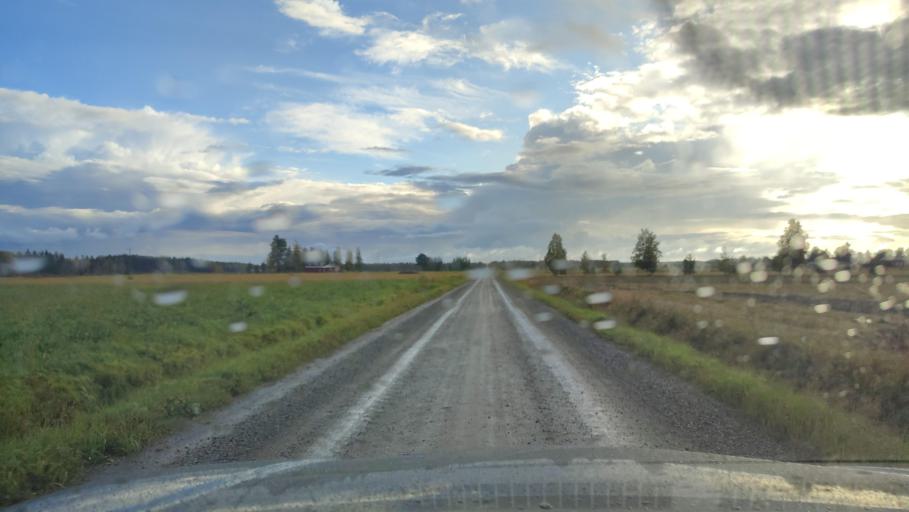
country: FI
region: Southern Ostrobothnia
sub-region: Suupohja
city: Karijoki
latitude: 62.3318
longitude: 21.5854
